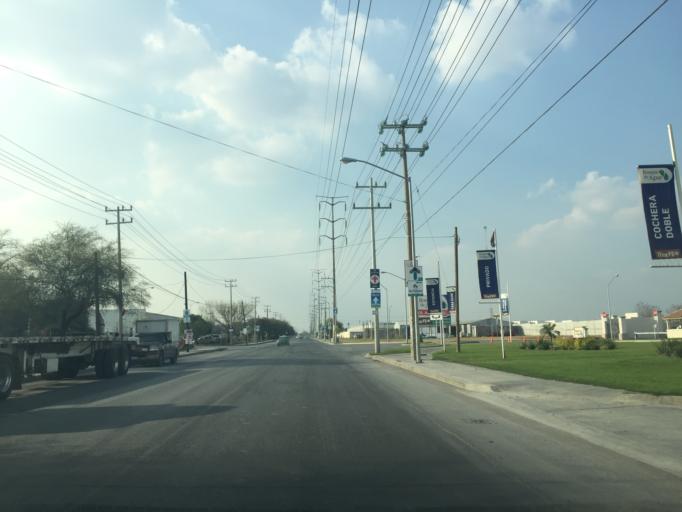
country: MX
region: Nuevo Leon
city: Apodaca
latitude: 25.7644
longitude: -100.2091
